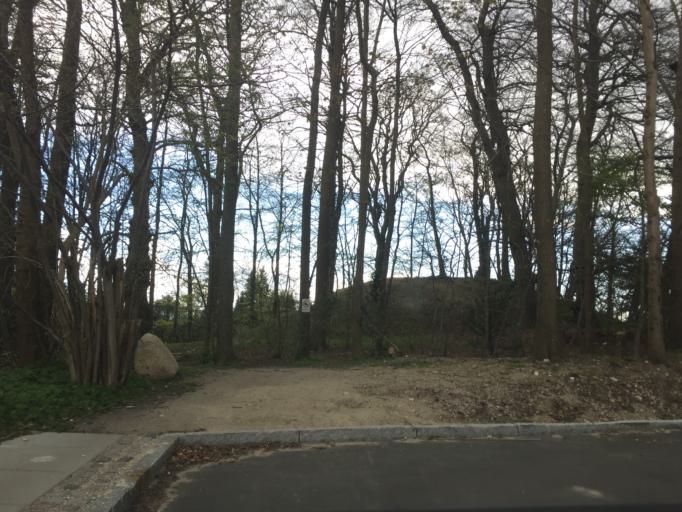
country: DK
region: Capital Region
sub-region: Gentofte Kommune
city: Charlottenlund
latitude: 55.7647
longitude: 12.5693
